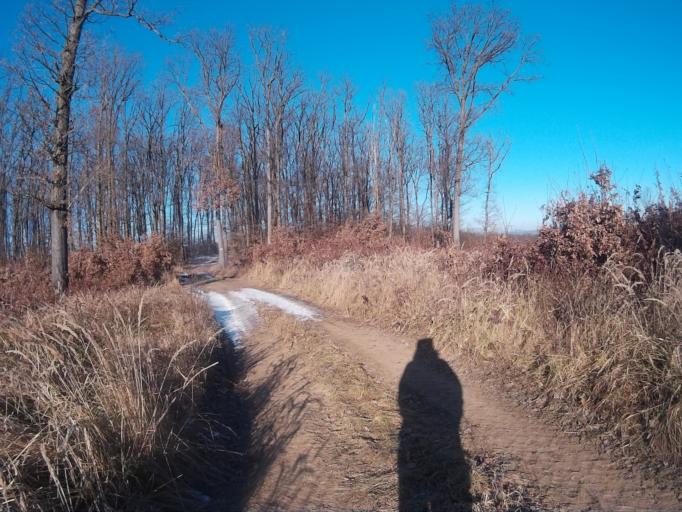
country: HU
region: Borsod-Abauj-Zemplen
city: Putnok
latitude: 48.4119
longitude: 20.4816
